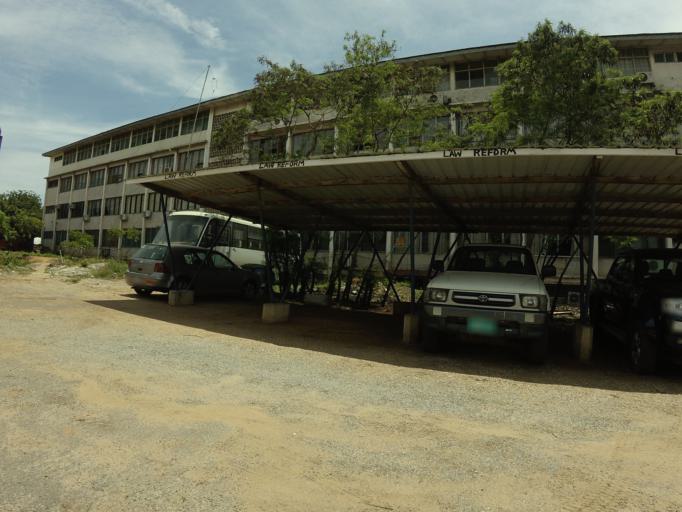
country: GH
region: Greater Accra
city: Accra
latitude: 5.5584
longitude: -0.2086
